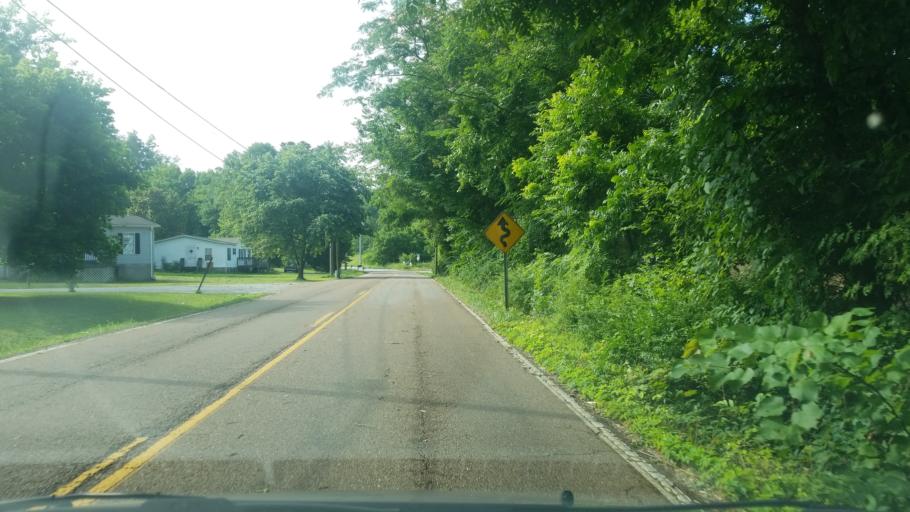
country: US
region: Tennessee
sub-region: Hamilton County
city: Apison
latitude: 35.0245
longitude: -85.0242
